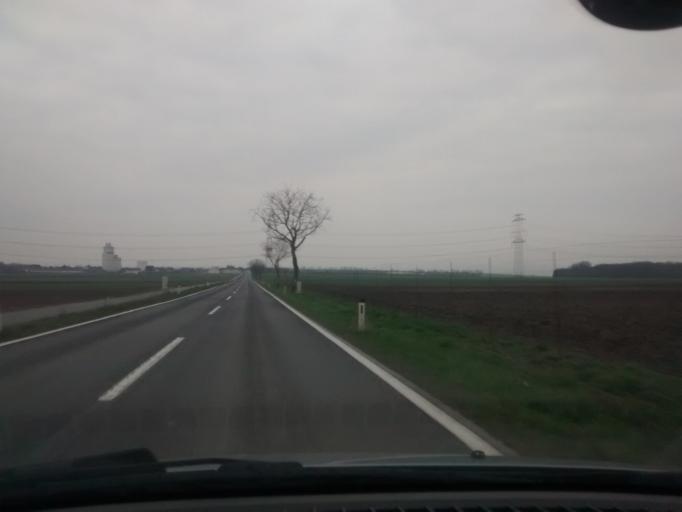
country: AT
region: Lower Austria
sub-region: Politischer Bezirk Wien-Umgebung
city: Ebergassing
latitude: 48.0421
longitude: 16.5076
